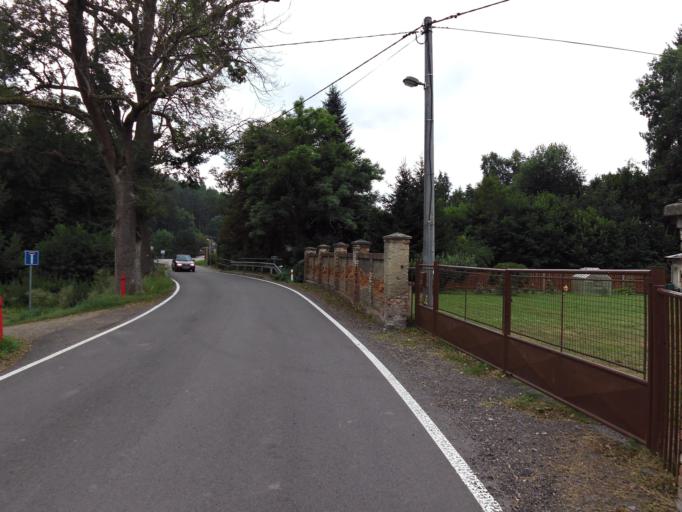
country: CZ
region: Central Bohemia
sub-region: Okres Benesov
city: Pysely
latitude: 49.8673
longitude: 14.6601
